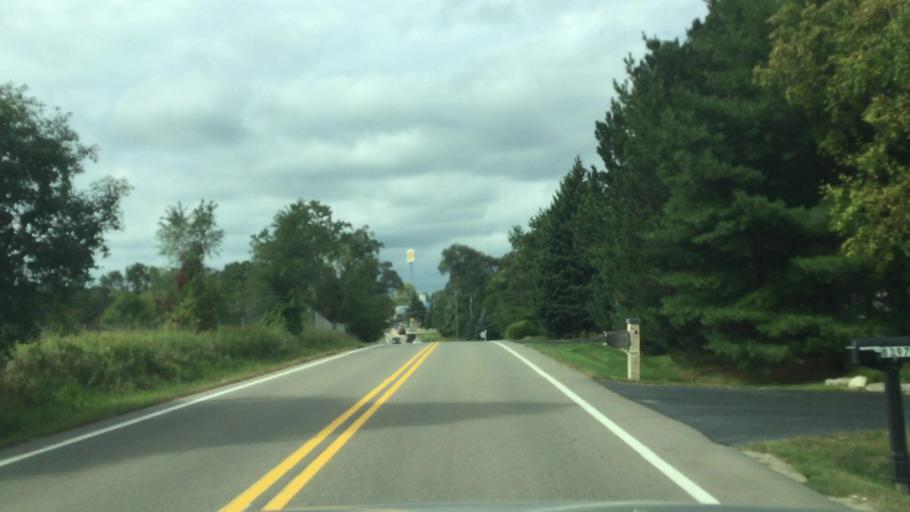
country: US
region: Michigan
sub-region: Livingston County
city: Brighton
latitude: 42.5499
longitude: -83.7842
